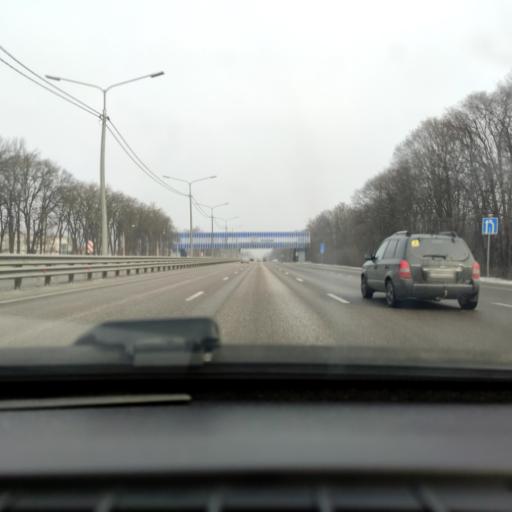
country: RU
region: Voronezj
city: Podgornoye
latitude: 51.8034
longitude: 39.2051
